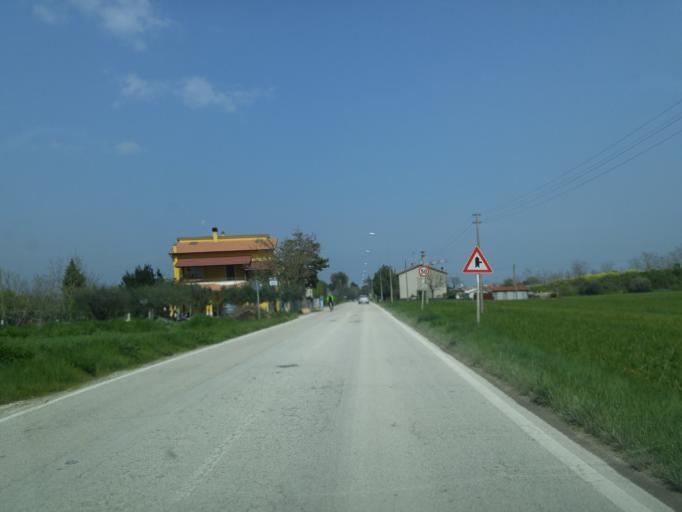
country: IT
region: The Marches
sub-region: Provincia di Pesaro e Urbino
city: Bellocchi
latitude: 43.7828
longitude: 12.9877
